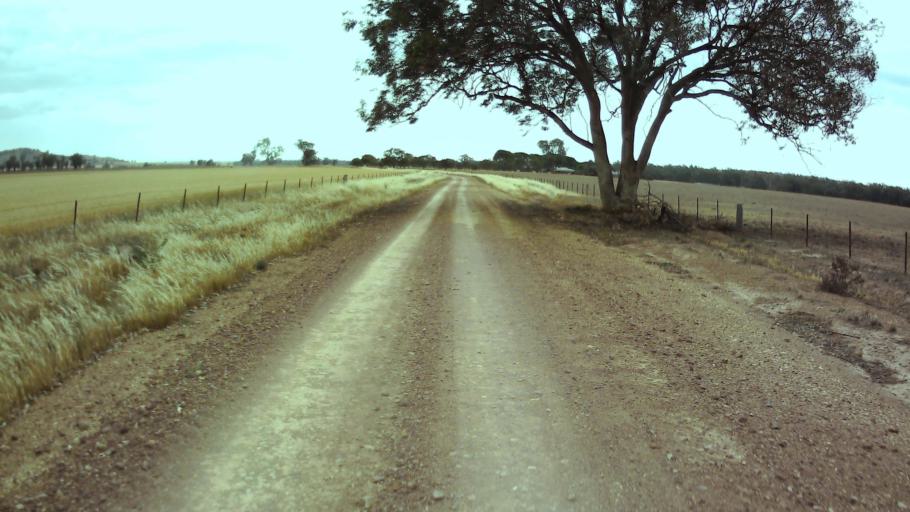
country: AU
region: New South Wales
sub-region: Weddin
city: Grenfell
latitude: -33.9188
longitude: 148.2865
